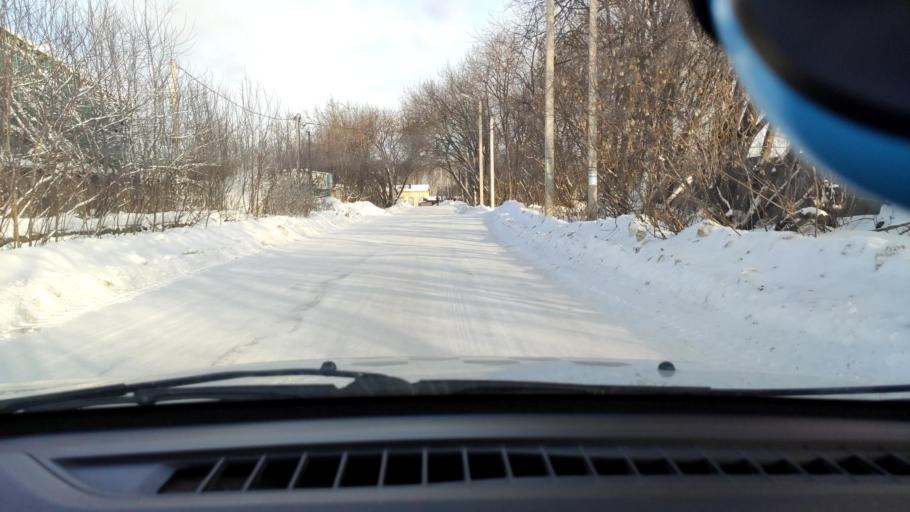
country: RU
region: Perm
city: Kultayevo
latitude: 57.9949
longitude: 55.9248
